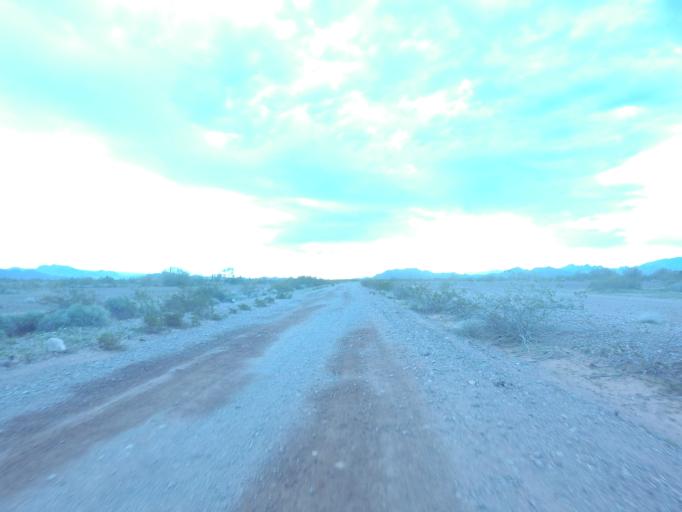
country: US
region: Arizona
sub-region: La Paz County
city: Quartzsite
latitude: 33.5370
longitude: -114.2142
